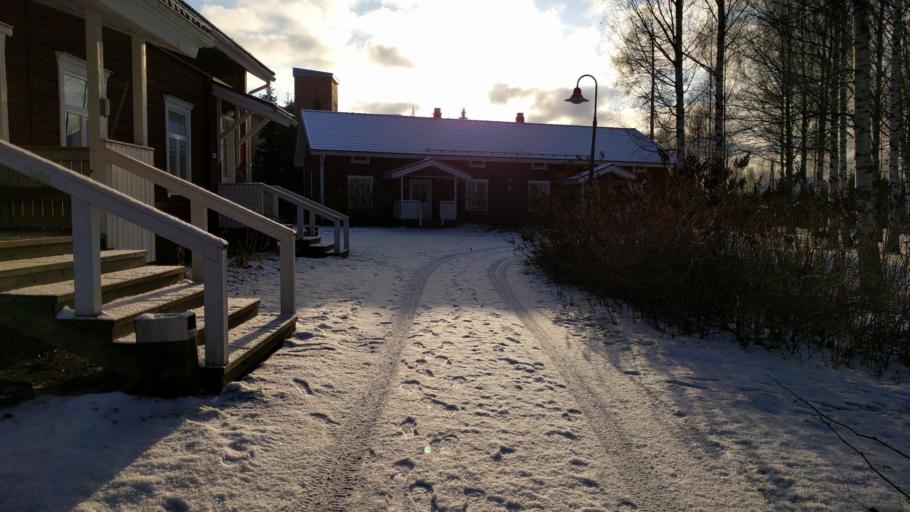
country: FI
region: Paijanne Tavastia
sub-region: Lahti
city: Heinola
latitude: 61.1672
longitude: 25.9874
